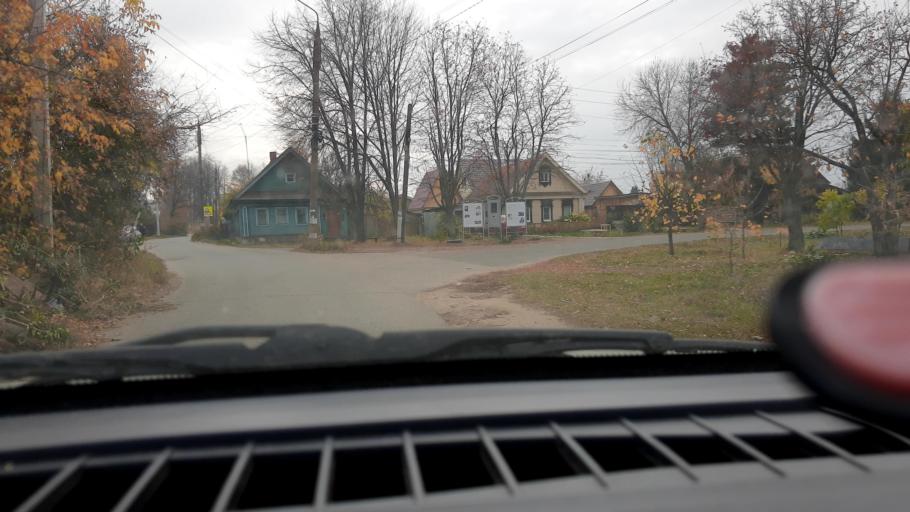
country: RU
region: Nizjnij Novgorod
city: Gorodets
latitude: 56.6391
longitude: 43.4700
